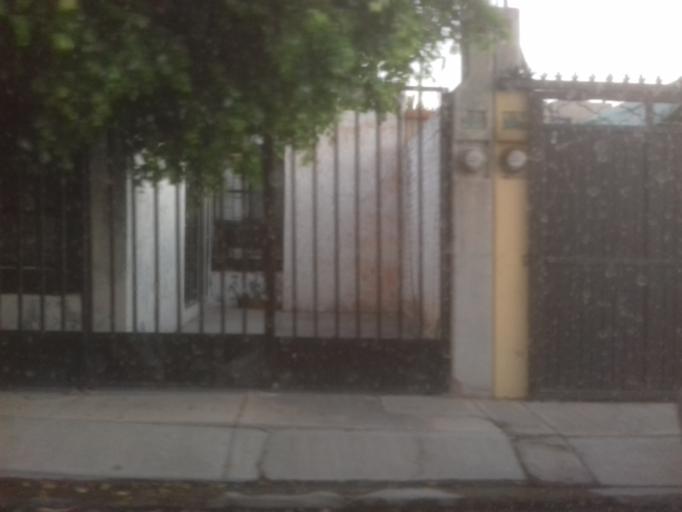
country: MX
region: Aguascalientes
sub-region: Aguascalientes
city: San Sebastian [Fraccionamiento]
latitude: 21.8507
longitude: -102.2604
